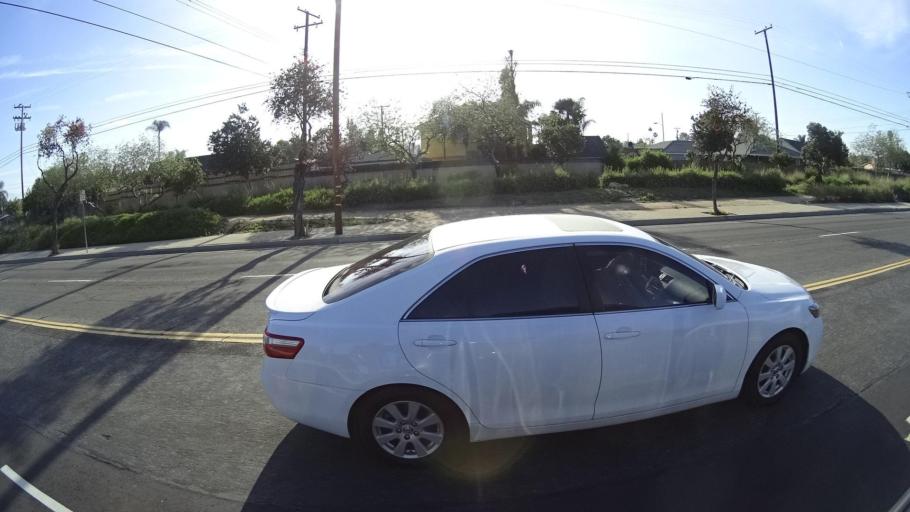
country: US
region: California
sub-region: Los Angeles County
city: Valinda
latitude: 34.0342
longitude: -117.9265
